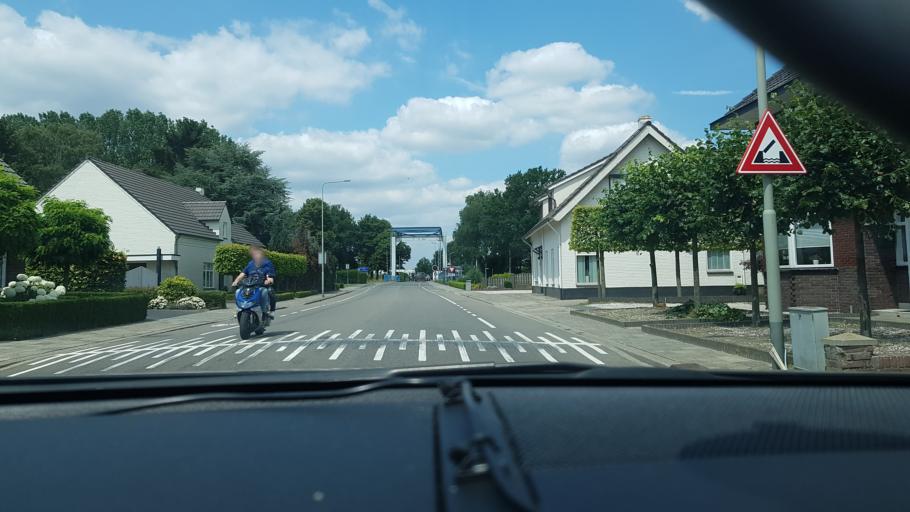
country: NL
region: Limburg
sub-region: Gemeente Nederweert
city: Nederweert
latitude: 51.2794
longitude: 5.7716
